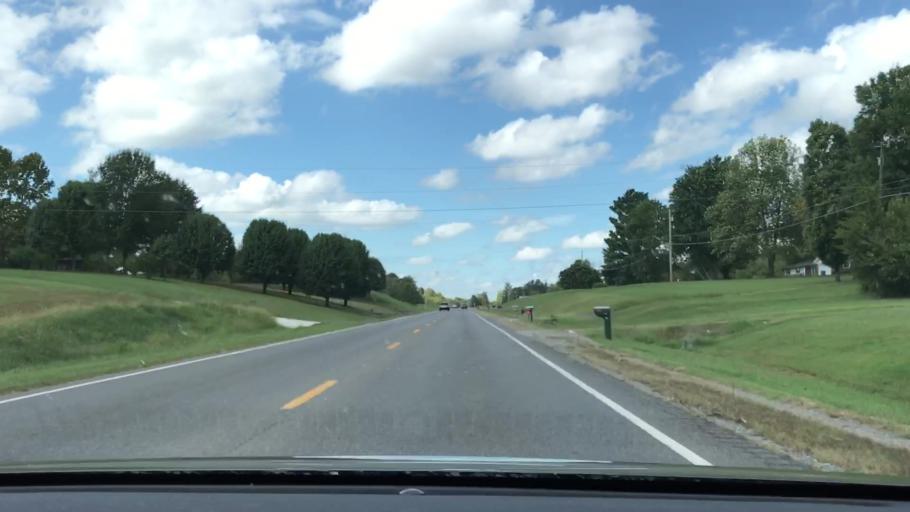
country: US
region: Kentucky
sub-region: Livingston County
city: Ledbetter
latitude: 37.0077
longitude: -88.4880
